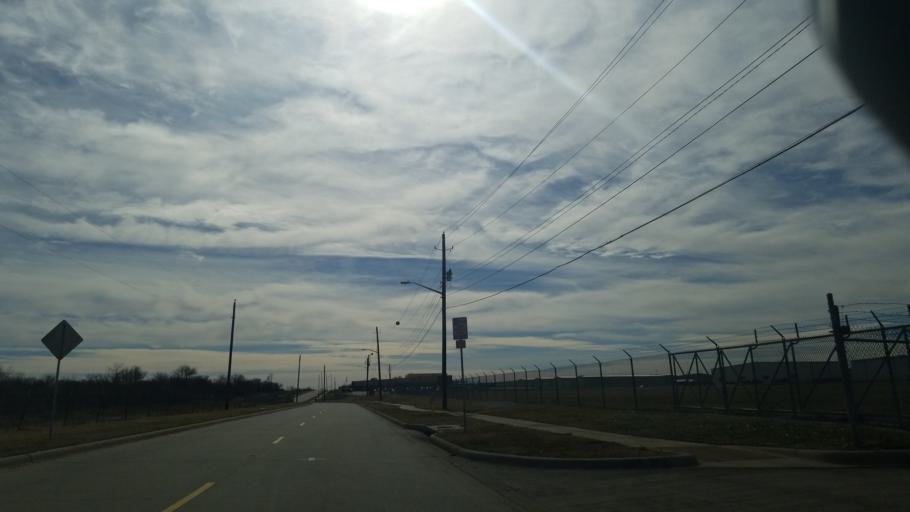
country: US
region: Texas
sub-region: Denton County
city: Denton
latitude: 33.1999
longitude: -97.1906
